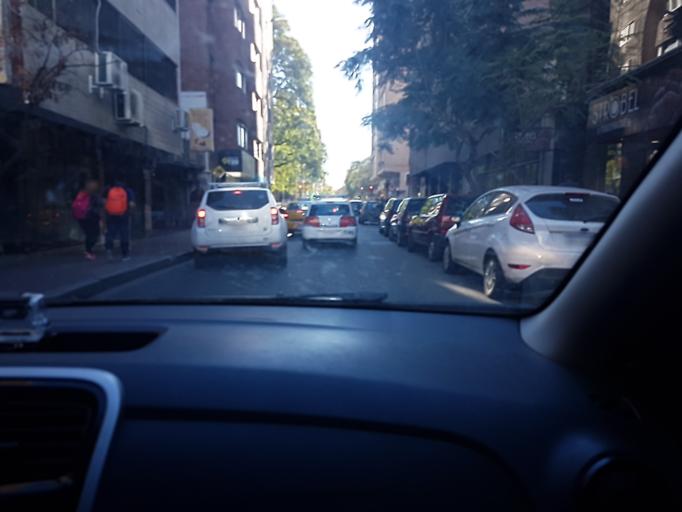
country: AR
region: Cordoba
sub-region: Departamento de Capital
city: Cordoba
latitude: -31.4182
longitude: -64.1889
